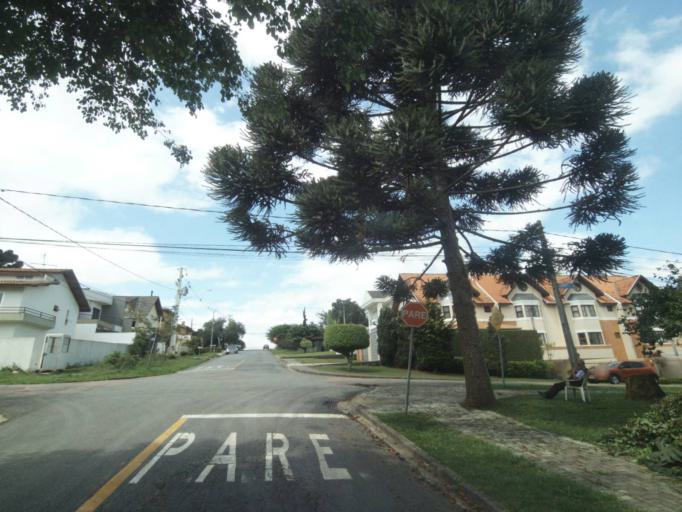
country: BR
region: Parana
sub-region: Pinhais
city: Pinhais
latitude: -25.4162
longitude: -49.2283
